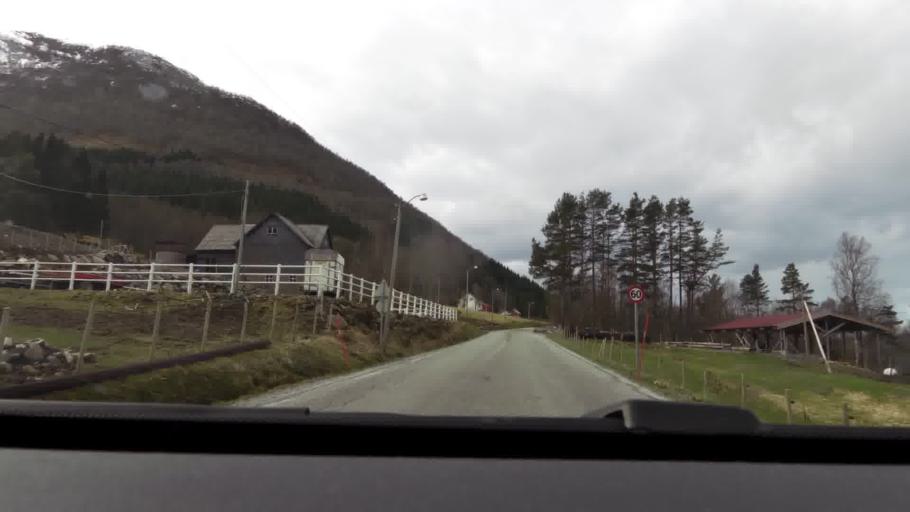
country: NO
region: More og Romsdal
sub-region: Gjemnes
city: Batnfjordsora
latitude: 62.9246
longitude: 7.5923
